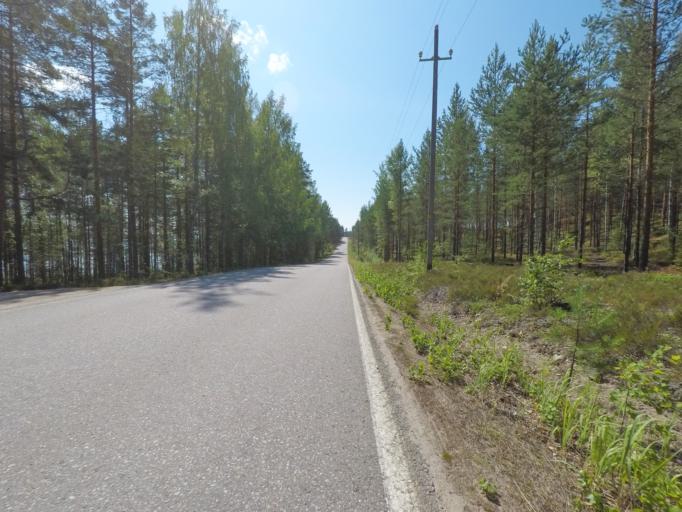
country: FI
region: Southern Savonia
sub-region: Mikkeli
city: Puumala
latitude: 61.4592
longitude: 28.1750
